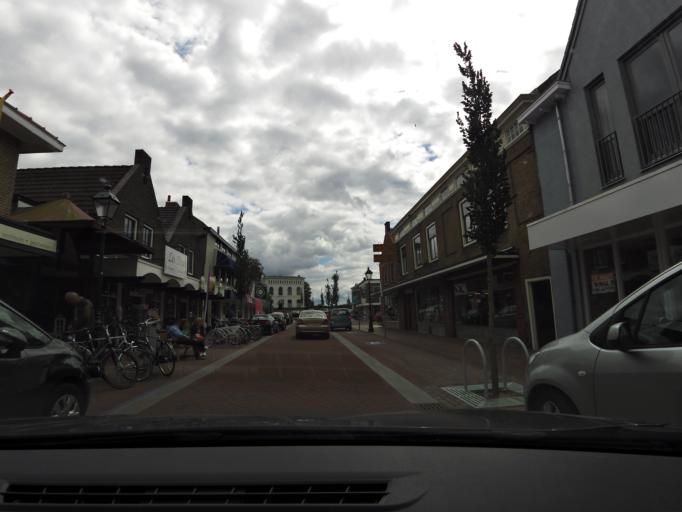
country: NL
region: North Brabant
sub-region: Gemeente Moerdijk
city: Willemstad
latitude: 51.7274
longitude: 4.4379
